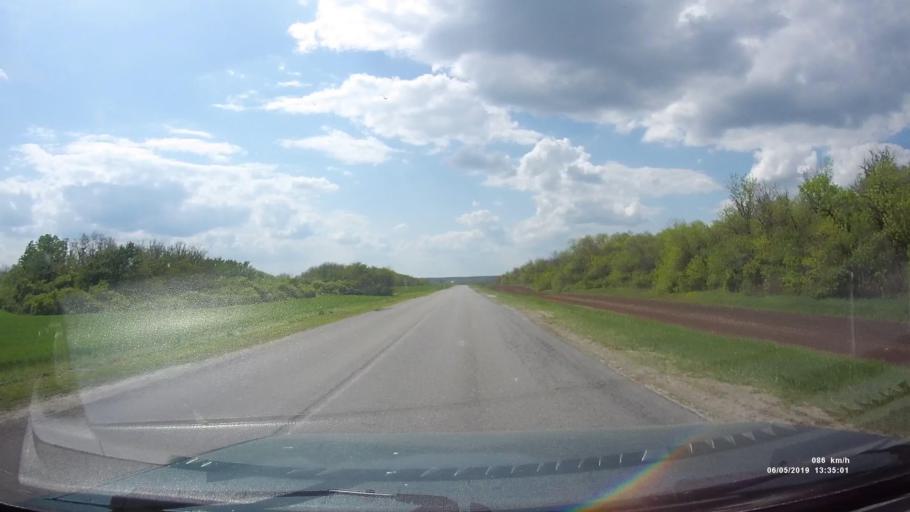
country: RU
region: Rostov
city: Ust'-Donetskiy
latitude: 47.6937
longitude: 40.7521
